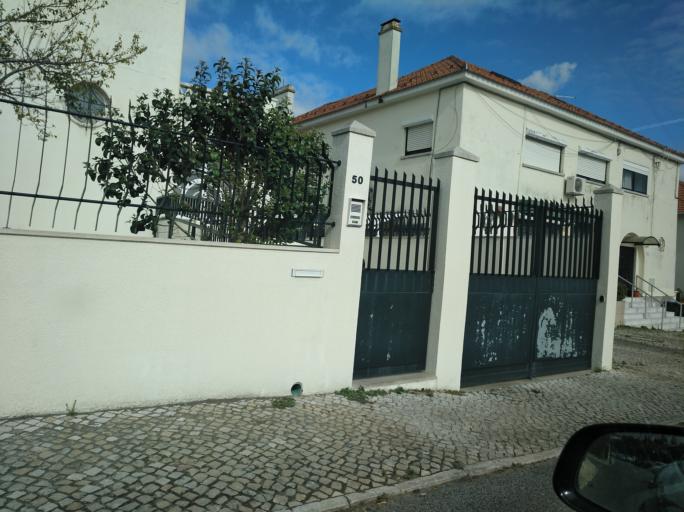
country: PT
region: Lisbon
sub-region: Loures
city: Moscavide
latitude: 38.7714
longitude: -9.1156
